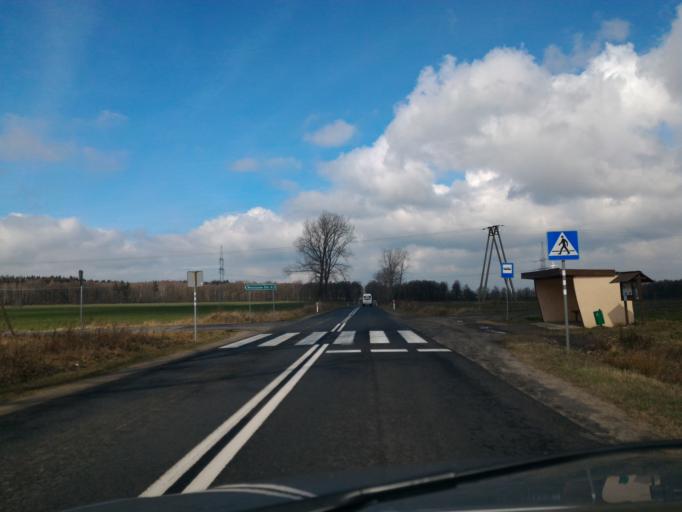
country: PL
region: Lower Silesian Voivodeship
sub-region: Powiat zgorzelecki
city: Sulikow
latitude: 51.0557
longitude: 15.0390
